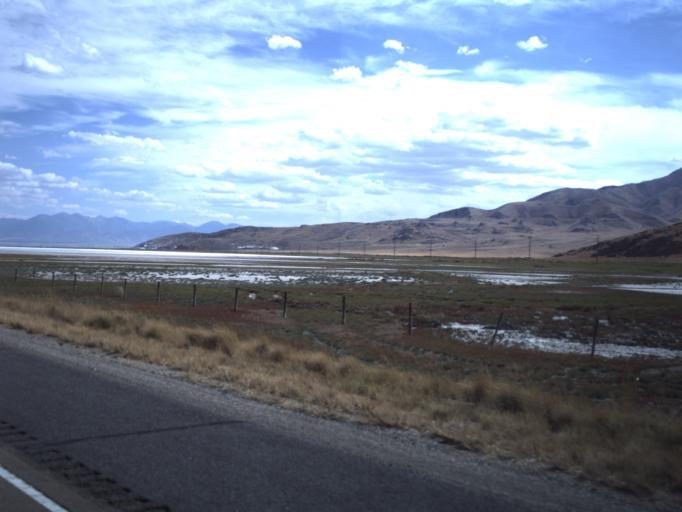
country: US
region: Utah
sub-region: Tooele County
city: Grantsville
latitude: 40.7397
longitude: -112.6229
